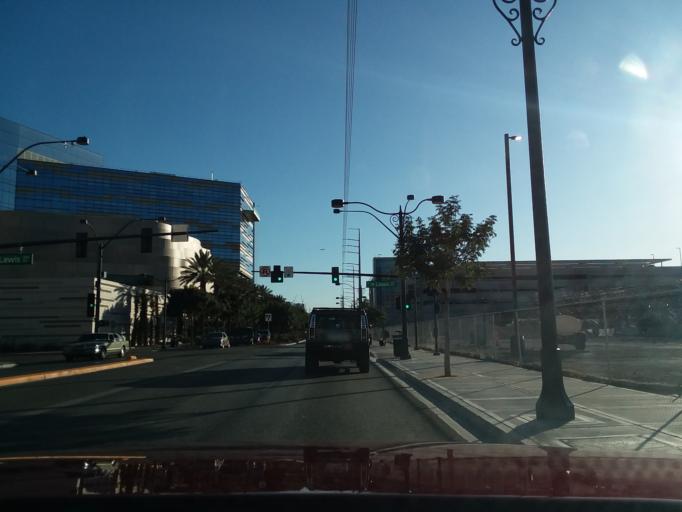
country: US
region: Nevada
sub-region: Clark County
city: Las Vegas
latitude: 36.1686
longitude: -115.1486
